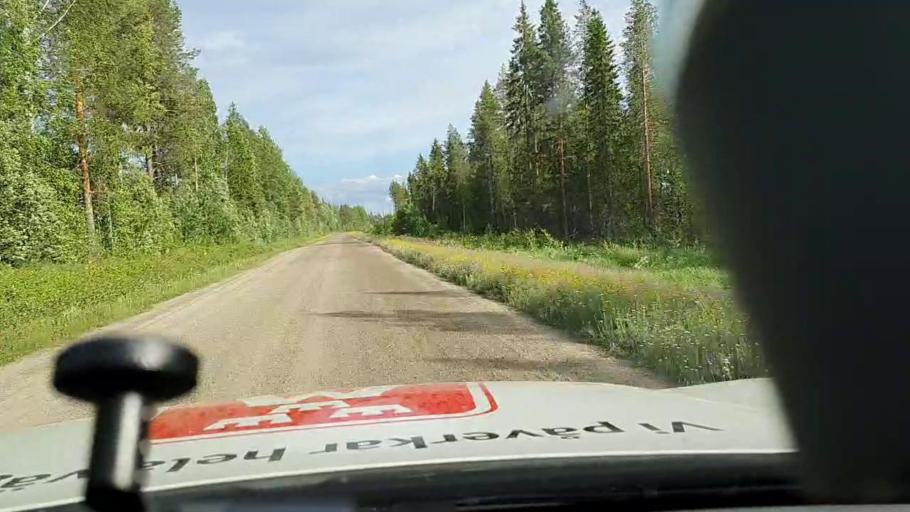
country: SE
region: Norrbotten
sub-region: Alvsbyns Kommun
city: AElvsbyn
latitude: 66.1789
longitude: 21.2328
